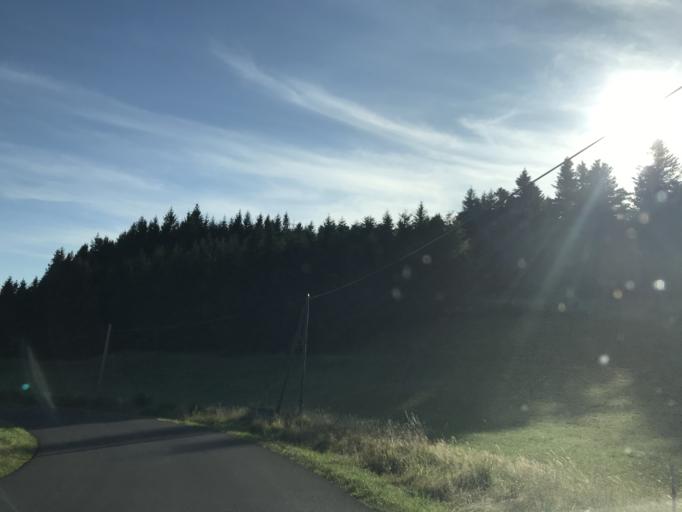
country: FR
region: Auvergne
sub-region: Departement du Puy-de-Dome
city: Job
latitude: 45.6786
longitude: 3.7479
